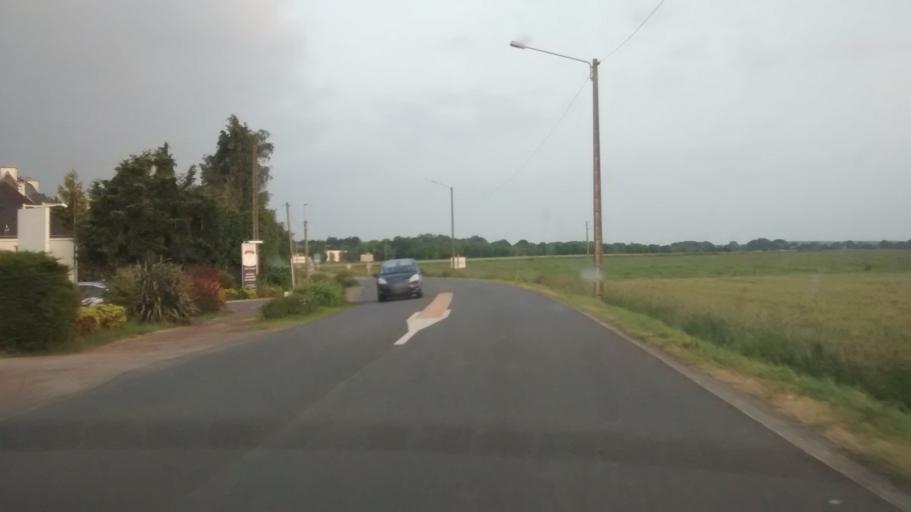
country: FR
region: Brittany
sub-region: Departement du Morbihan
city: Guer
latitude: 47.9355
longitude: -2.1301
